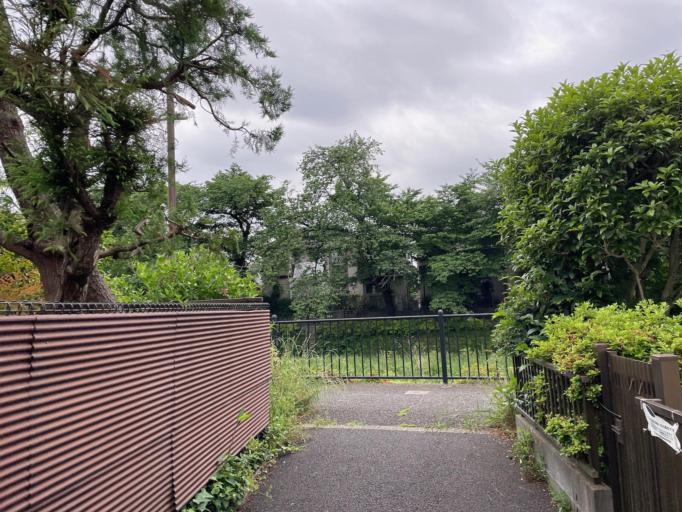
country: JP
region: Tokyo
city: Chofugaoka
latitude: 35.6581
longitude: 139.5548
